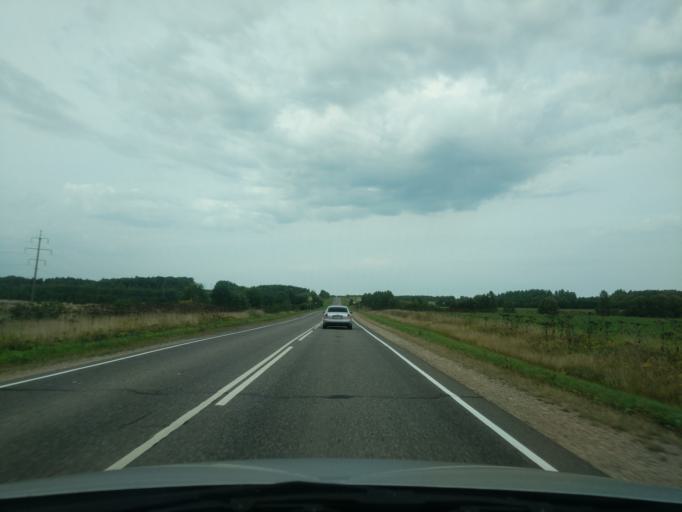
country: RU
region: Kirov
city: Mirnyy
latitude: 58.2727
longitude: 47.7875
